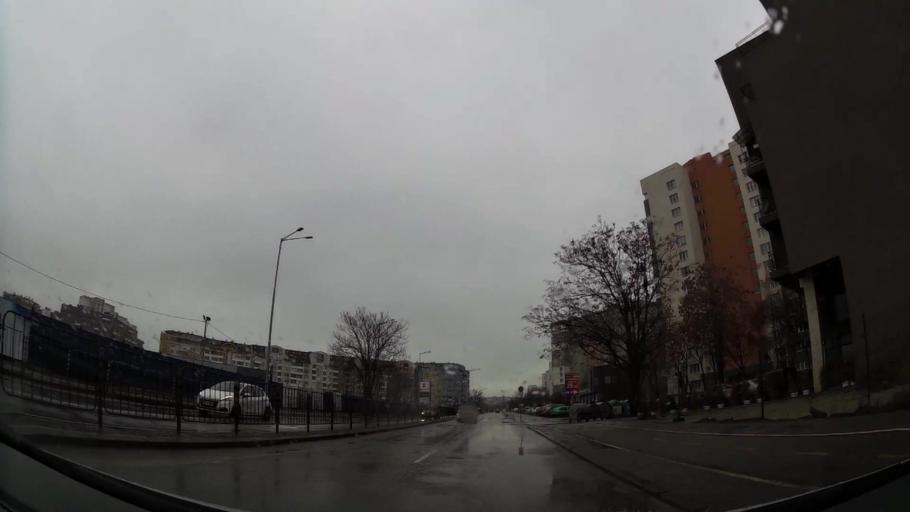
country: BG
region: Sofia-Capital
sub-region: Stolichna Obshtina
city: Sofia
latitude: 42.6461
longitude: 23.3773
